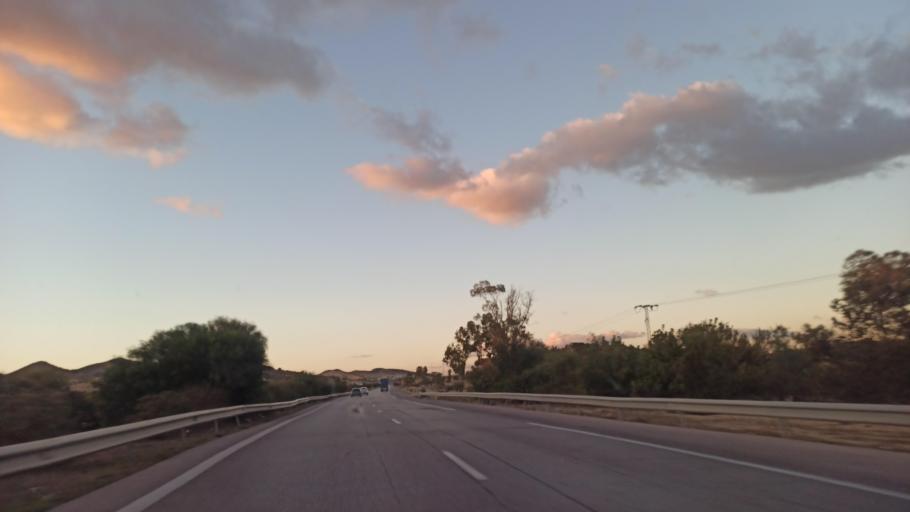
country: TN
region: Susah
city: Harqalah
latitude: 36.2172
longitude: 10.4197
